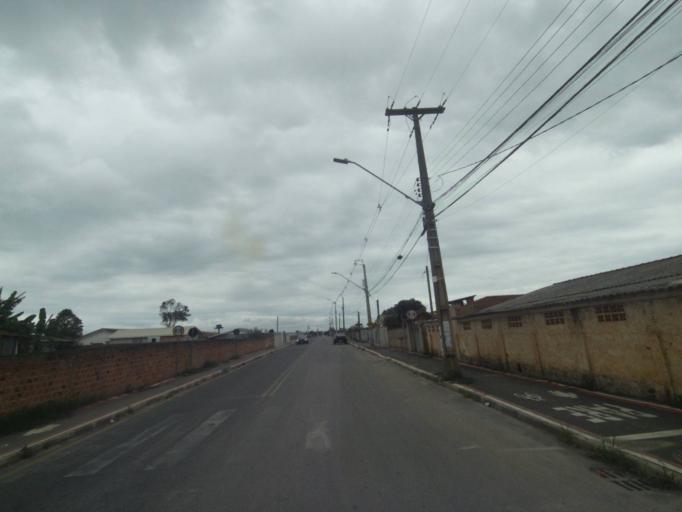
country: BR
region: Parana
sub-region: Quatro Barras
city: Quatro Barras
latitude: -25.3551
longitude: -49.1036
